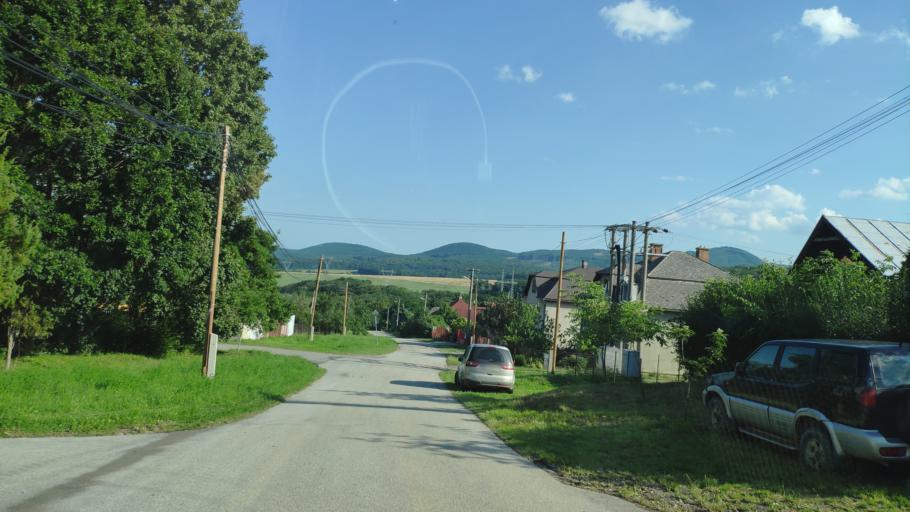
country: SK
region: Kosicky
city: Secovce
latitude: 48.6335
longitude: 21.4757
